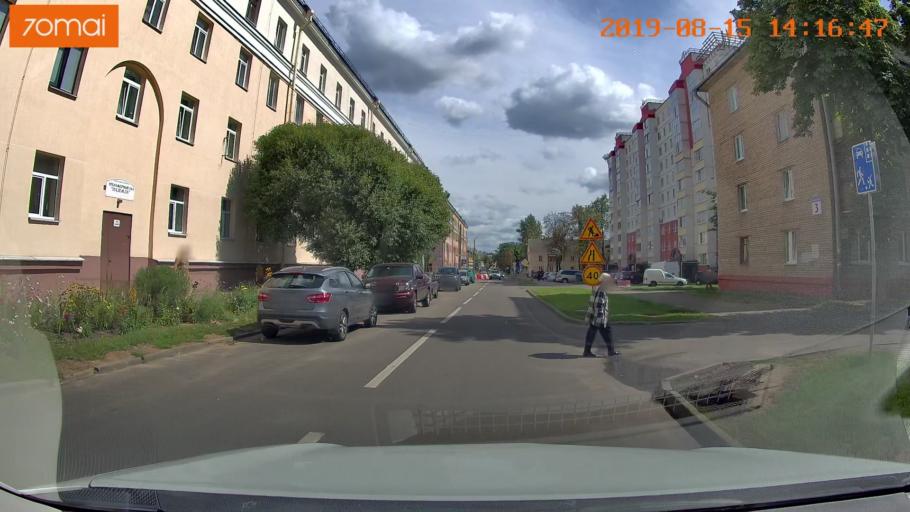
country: BY
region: Minsk
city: Minsk
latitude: 53.8852
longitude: 27.5929
